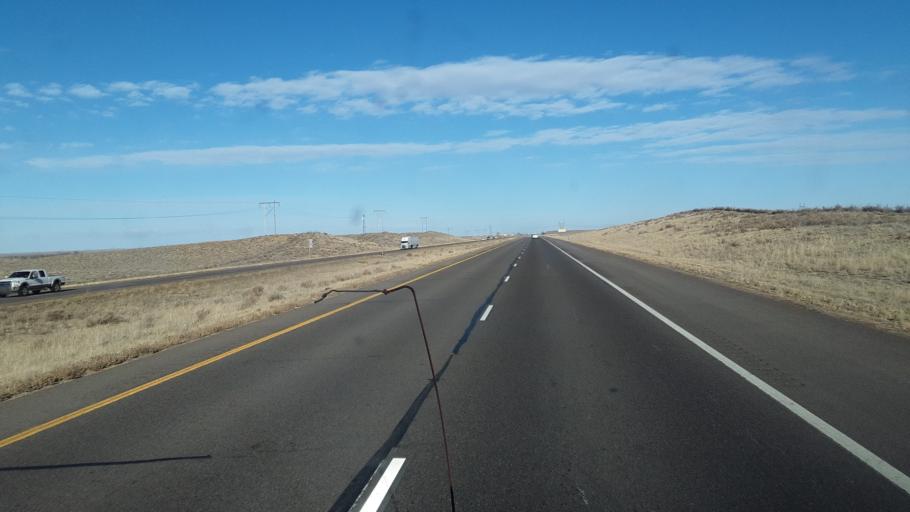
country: US
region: Colorado
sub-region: Morgan County
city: Brush
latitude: 40.2803
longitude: -103.5631
